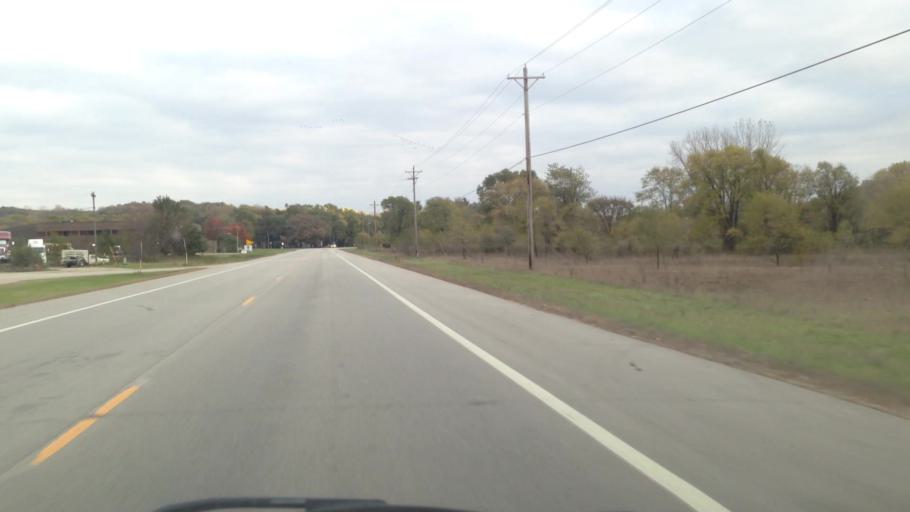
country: US
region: Minnesota
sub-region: Olmsted County
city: Rochester
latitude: 43.9868
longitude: -92.4084
